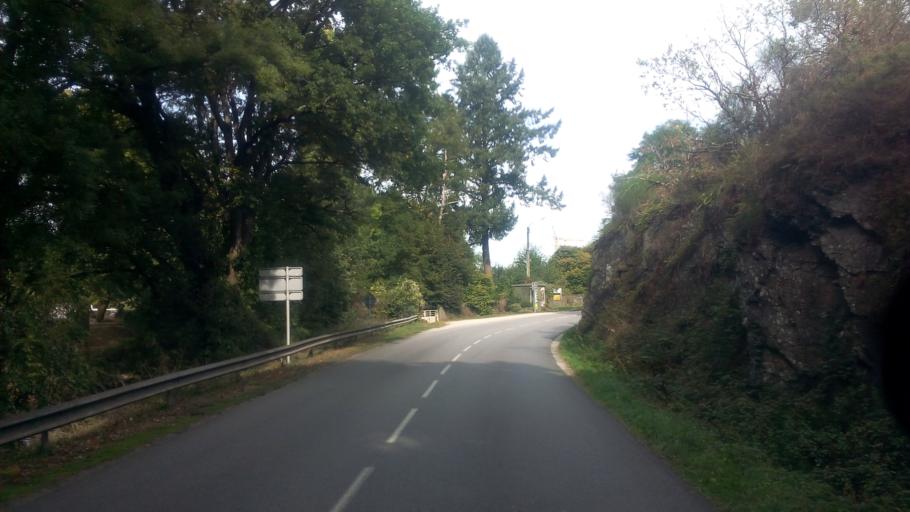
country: FR
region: Brittany
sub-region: Departement du Morbihan
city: La Gacilly
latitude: 47.7592
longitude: -2.1296
